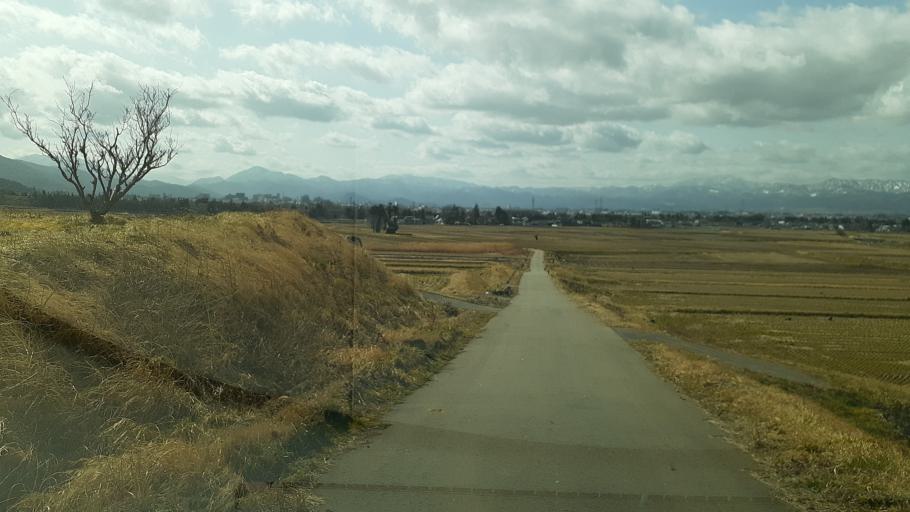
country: JP
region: Fukushima
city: Kitakata
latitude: 37.5352
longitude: 139.9413
